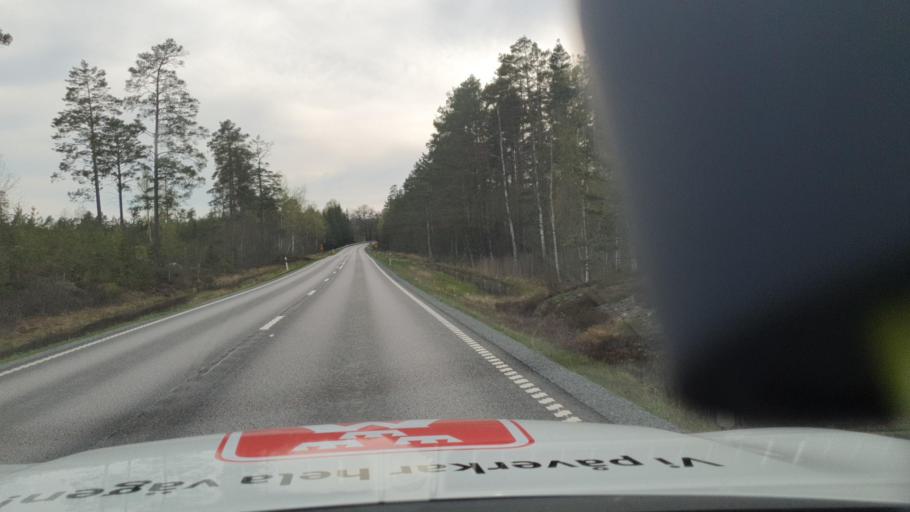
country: SE
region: Soedermanland
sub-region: Flens Kommun
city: Malmkoping
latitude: 59.2061
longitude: 16.8337
